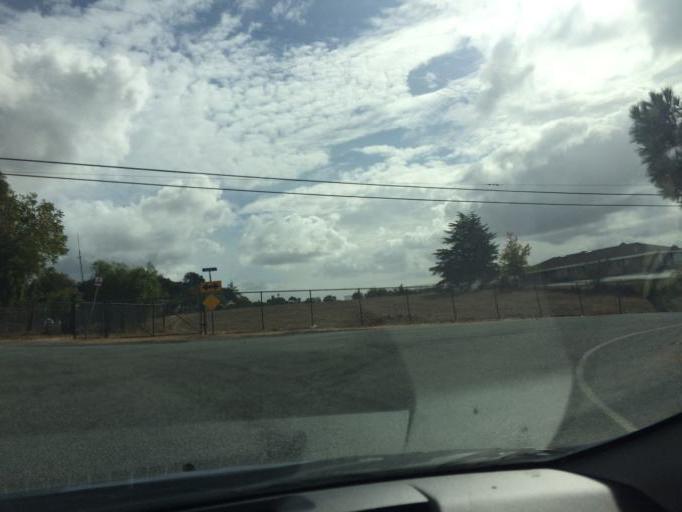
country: US
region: California
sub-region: Santa Clara County
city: Alum Rock
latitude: 37.3447
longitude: -121.7812
